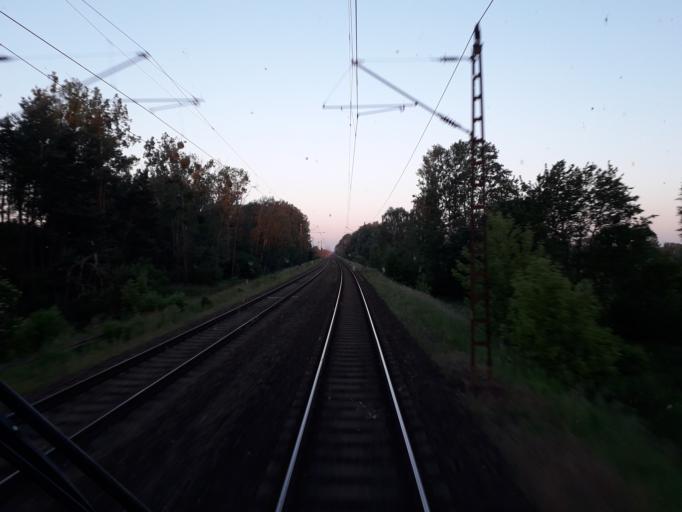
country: DE
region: Brandenburg
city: Hennigsdorf
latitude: 52.6546
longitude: 13.1787
